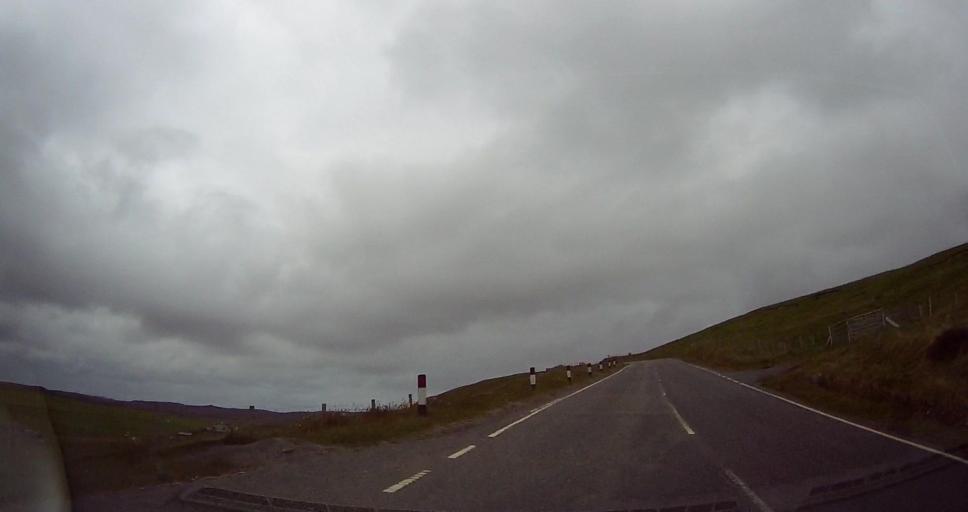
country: GB
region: Scotland
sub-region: Shetland Islands
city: Lerwick
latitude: 60.2558
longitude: -1.4071
